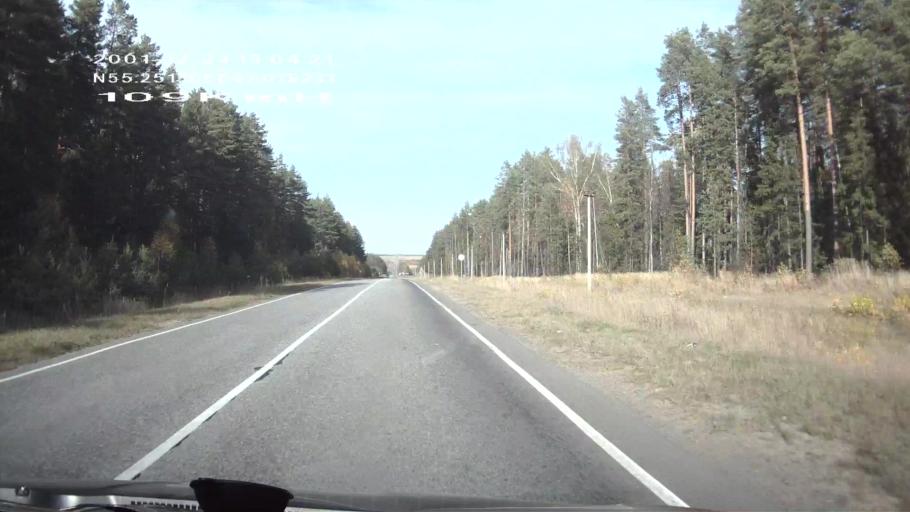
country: RU
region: Chuvashia
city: Buinsk
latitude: 55.2517
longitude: 47.0792
